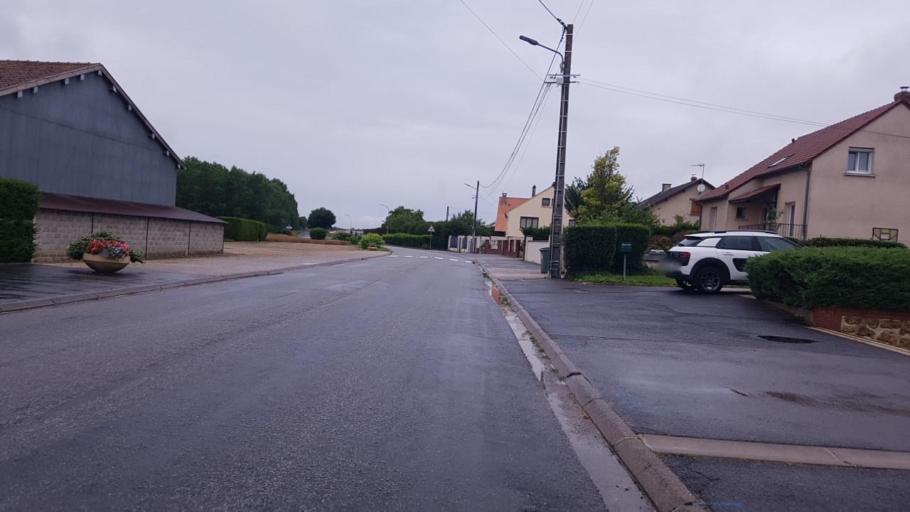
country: FR
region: Champagne-Ardenne
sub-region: Departement de la Marne
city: Sarry
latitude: 48.9094
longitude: 4.4254
